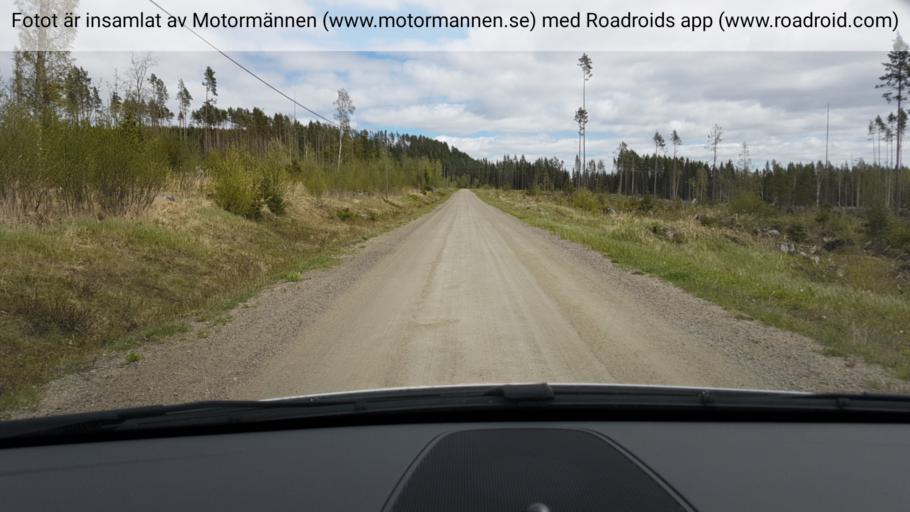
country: SE
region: Jaemtland
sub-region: OEstersunds Kommun
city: Brunflo
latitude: 62.8165
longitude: 15.0419
